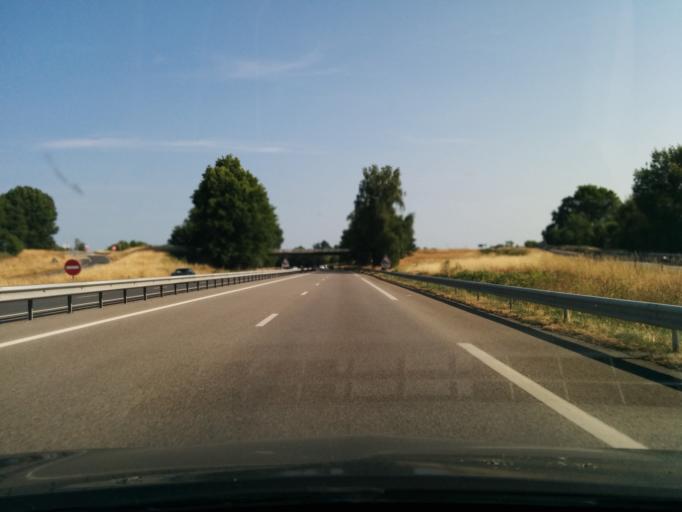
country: FR
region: Limousin
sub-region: Departement de la Haute-Vienne
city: Boisseuil
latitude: 45.7571
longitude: 1.3318
